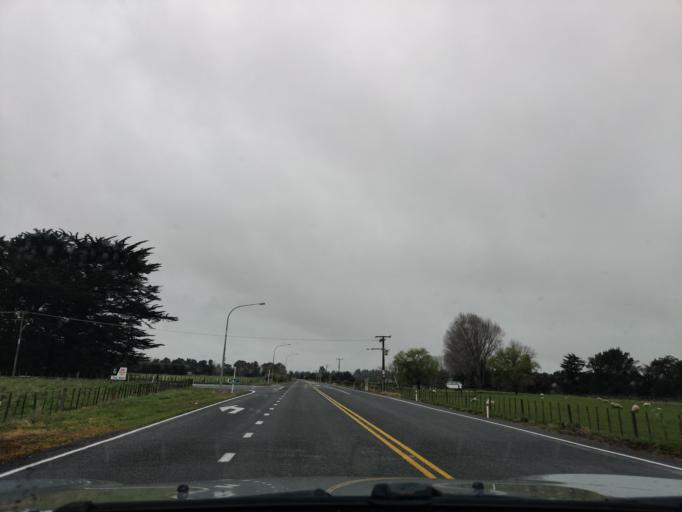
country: NZ
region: Hawke's Bay
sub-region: Hastings District
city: Hastings
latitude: -40.0210
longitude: 176.3233
